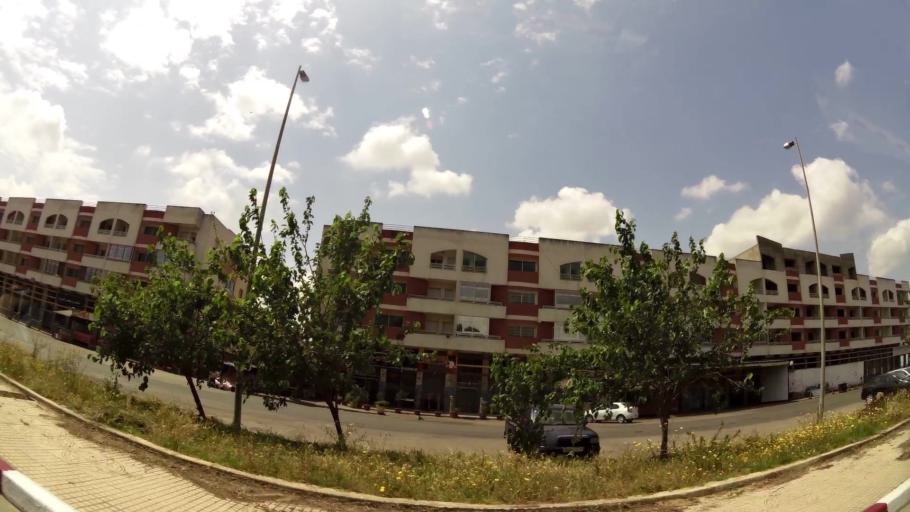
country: MA
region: Gharb-Chrarda-Beni Hssen
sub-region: Kenitra Province
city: Kenitra
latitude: 34.0122
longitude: -6.5381
